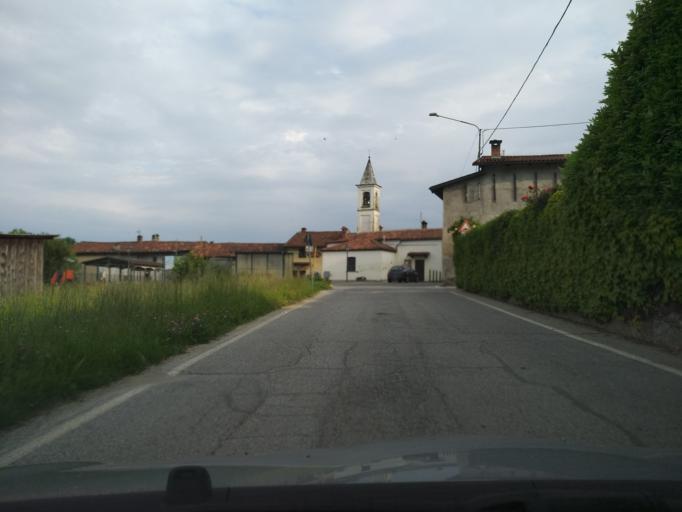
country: IT
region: Piedmont
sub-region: Provincia di Torino
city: Roletto
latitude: 44.9139
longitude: 7.3359
